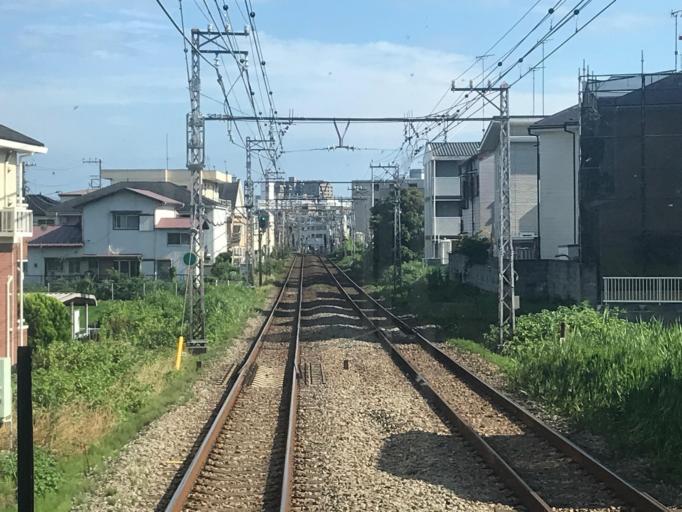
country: JP
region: Kanagawa
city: Odawara
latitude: 35.2942
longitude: 139.1462
